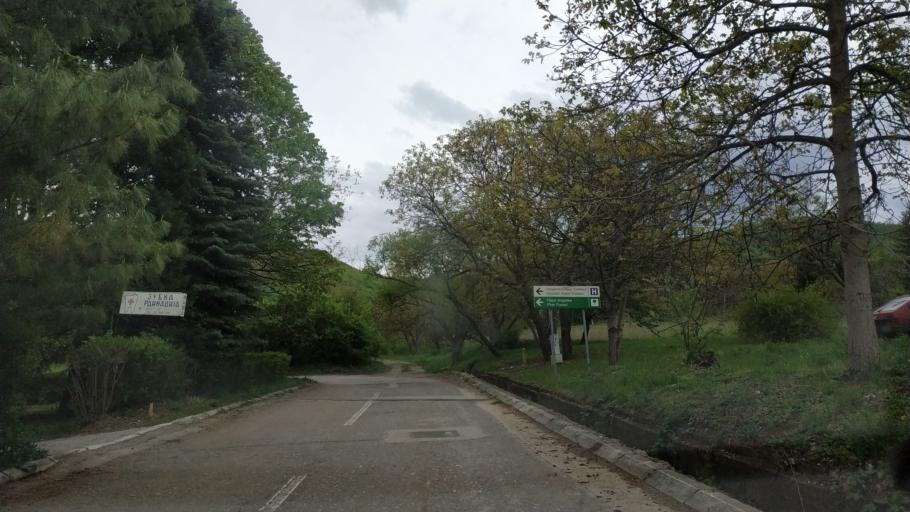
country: RS
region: Central Serbia
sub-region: Zajecarski Okrug
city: Soko Banja
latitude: 43.6406
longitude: 21.8654
